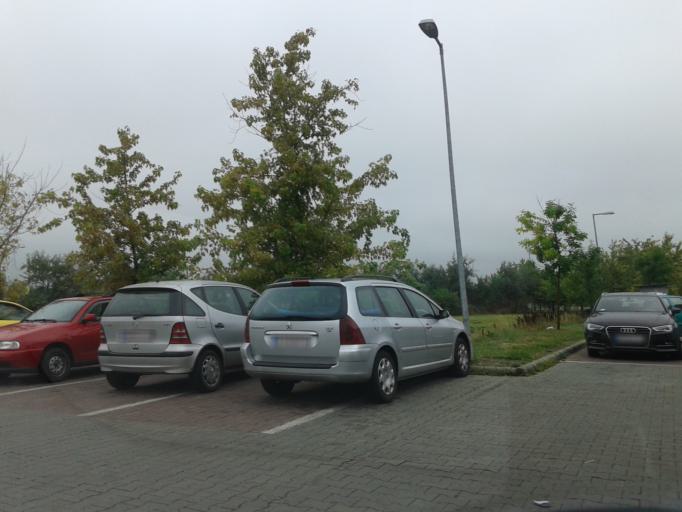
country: HU
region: Csongrad
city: Szeged
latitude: 46.2429
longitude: 20.1264
